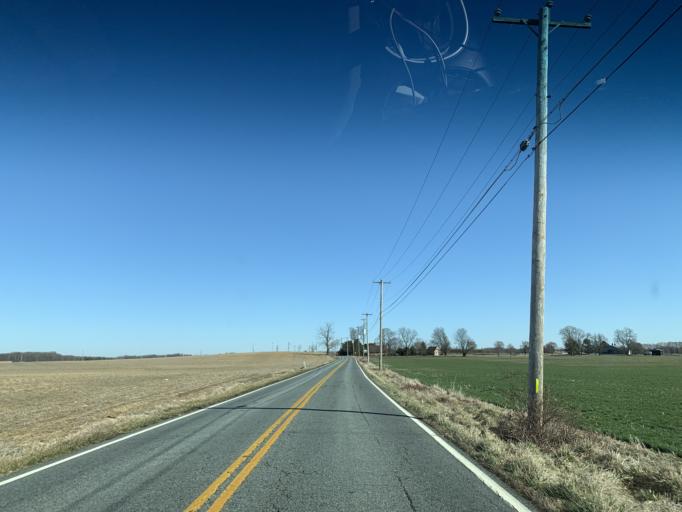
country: US
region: Maryland
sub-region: Cecil County
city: Elkton
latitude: 39.4896
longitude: -75.8615
